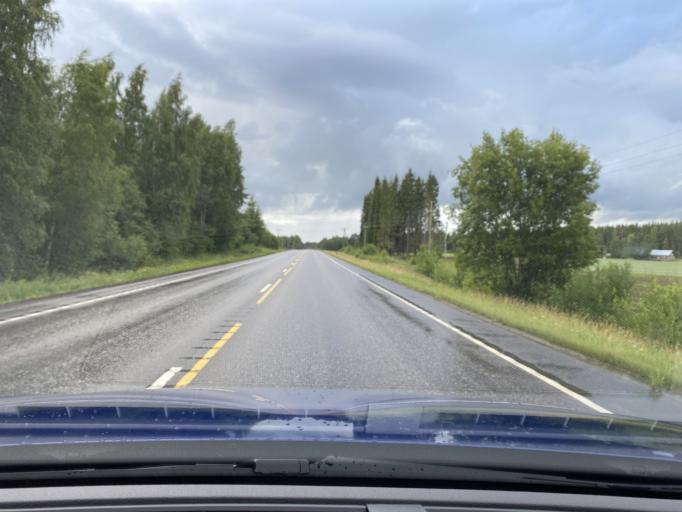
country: FI
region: Uusimaa
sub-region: Helsinki
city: Nurmijaervi
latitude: 60.5480
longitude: 24.8286
